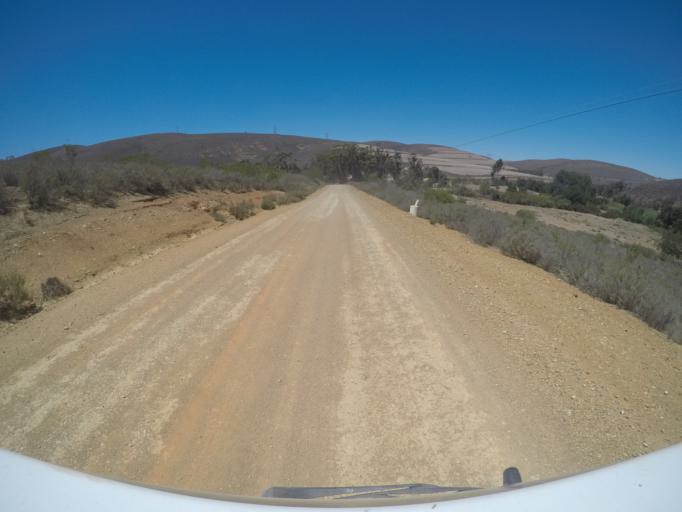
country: ZA
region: Western Cape
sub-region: Overberg District Municipality
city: Caledon
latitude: -34.1365
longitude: 19.2460
